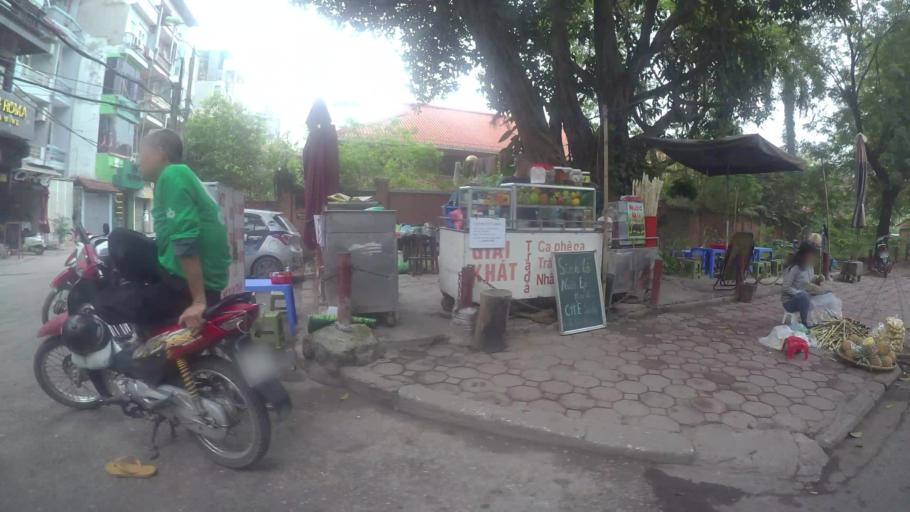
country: VN
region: Ha Noi
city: Dong Da
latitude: 21.0323
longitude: 105.8210
